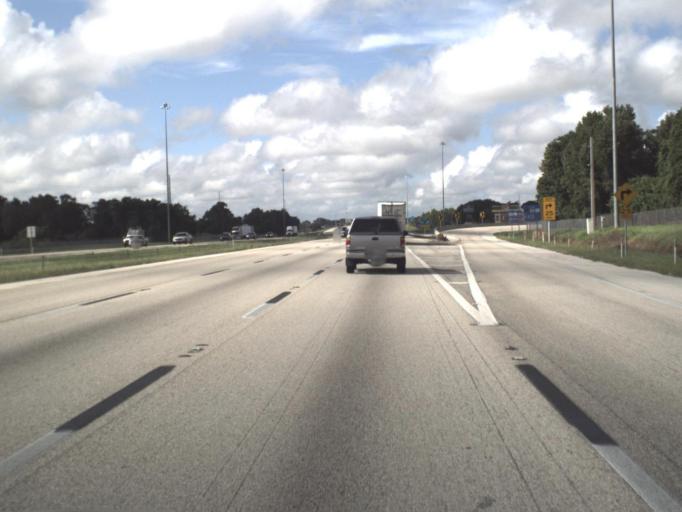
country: US
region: Florida
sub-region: Polk County
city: Gibsonia
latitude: 28.1050
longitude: -81.9463
